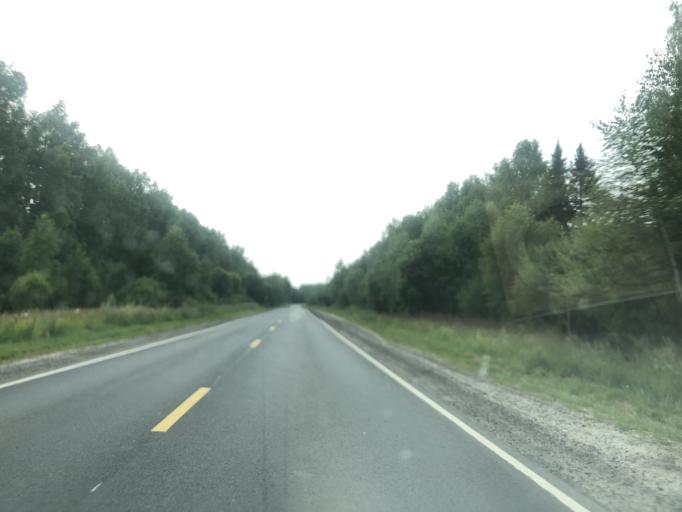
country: RU
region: Ivanovo
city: Verkhniy Landekh
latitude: 56.7735
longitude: 42.4090
